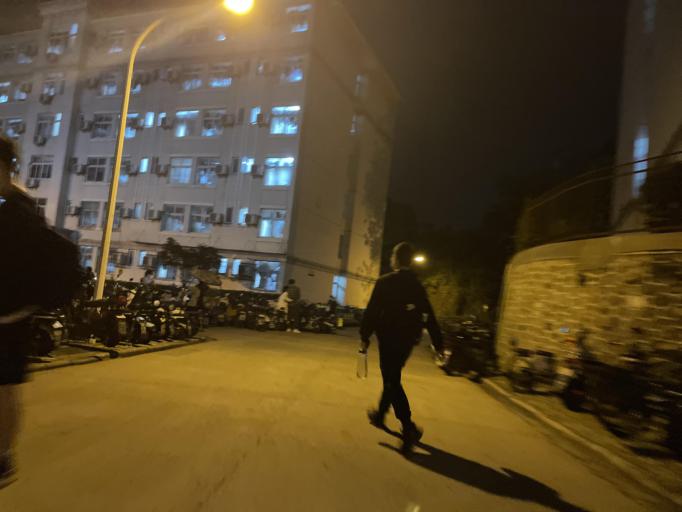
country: CN
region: Hubei
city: Guanshan
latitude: 30.5182
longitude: 114.4282
